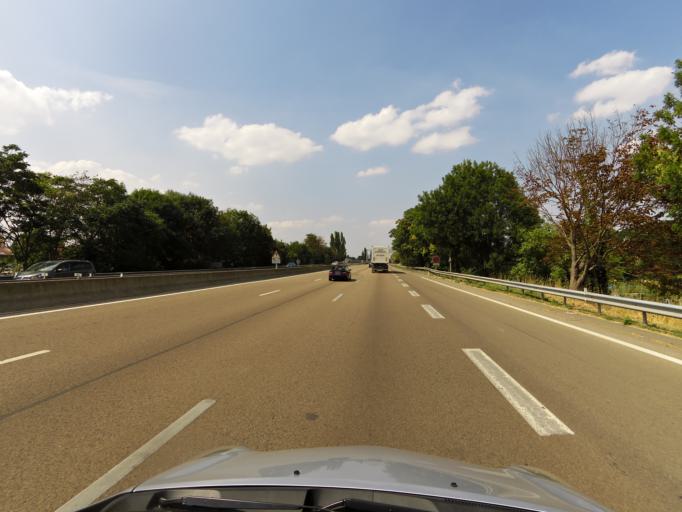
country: FR
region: Champagne-Ardenne
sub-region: Departement de la Marne
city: Reims
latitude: 49.2370
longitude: 4.0371
